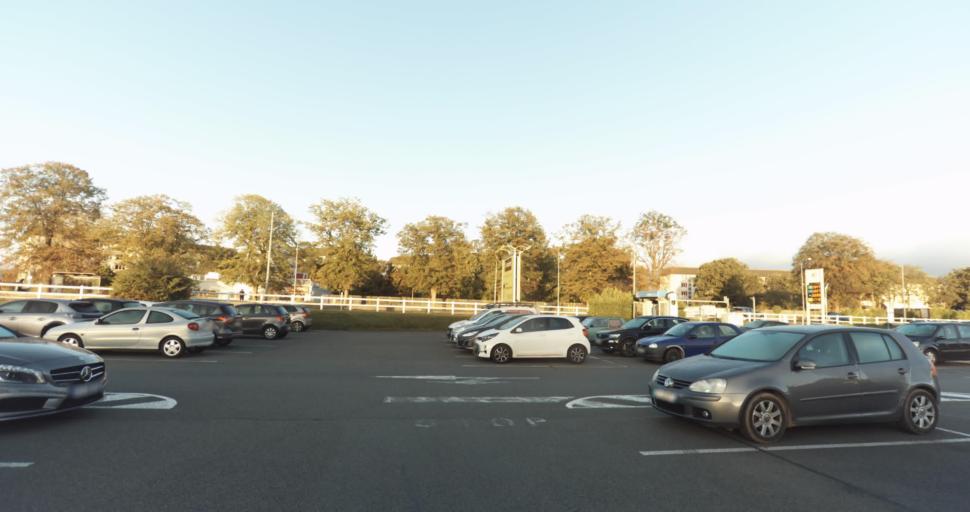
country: FR
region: Centre
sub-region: Departement d'Eure-et-Loir
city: Vernouillet
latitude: 48.7161
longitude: 1.3680
